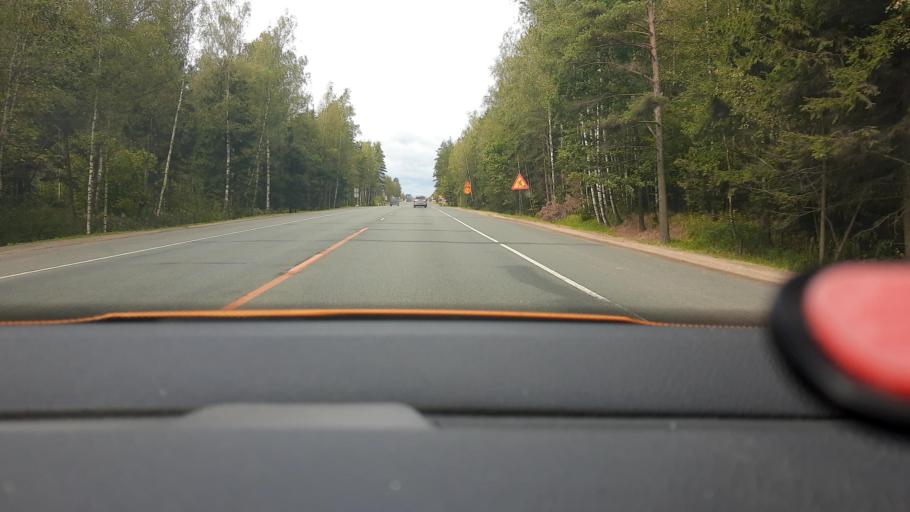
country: RU
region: Moskovskaya
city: Zelenogradskiy
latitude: 56.1001
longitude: 37.9716
